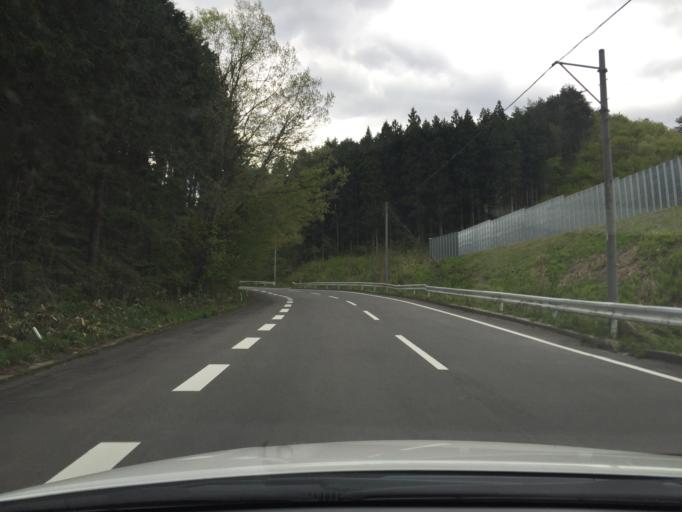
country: JP
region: Fukushima
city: Yanagawamachi-saiwaicho
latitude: 37.7522
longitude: 140.6909
